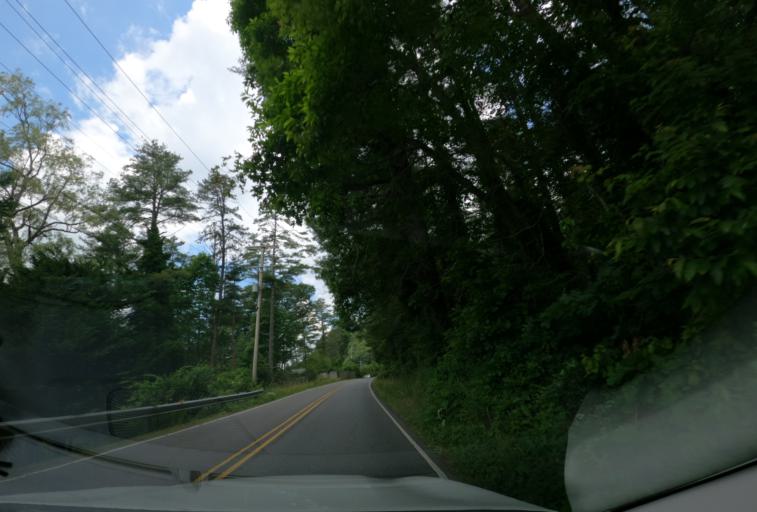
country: US
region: North Carolina
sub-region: Macon County
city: Franklin
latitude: 35.0663
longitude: -83.2223
